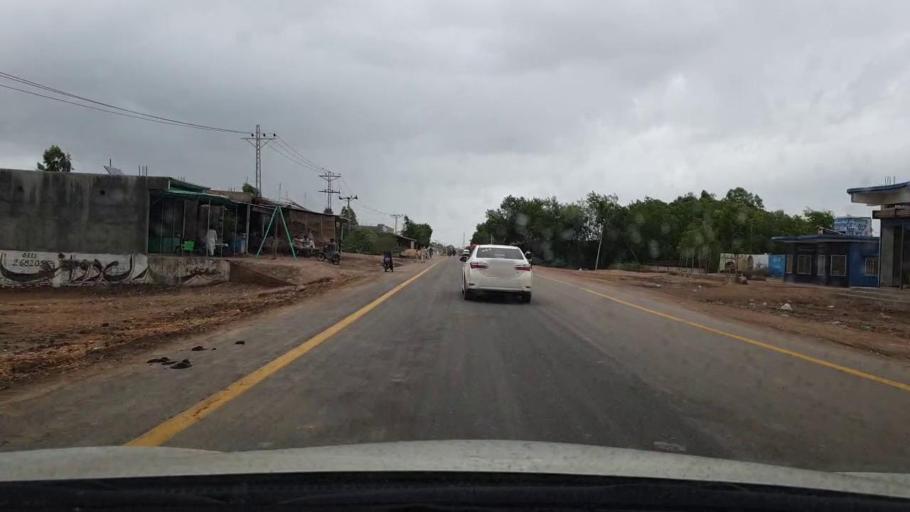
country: PK
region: Sindh
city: Badin
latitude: 24.6553
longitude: 68.8179
